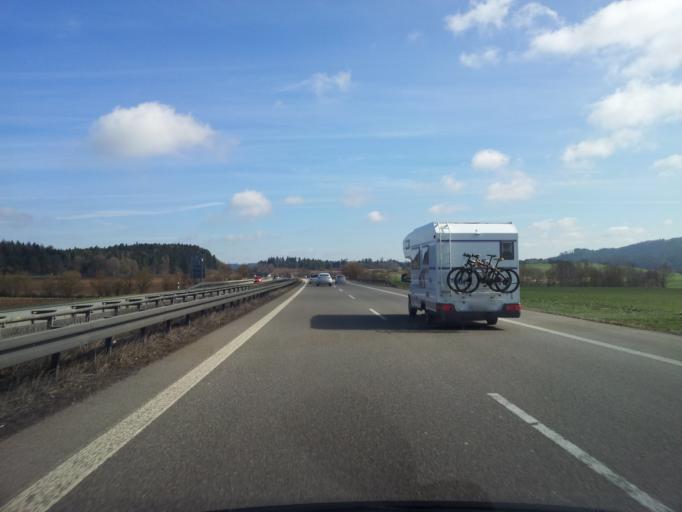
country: DE
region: Baden-Wuerttemberg
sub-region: Freiburg Region
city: Dietingen
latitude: 48.2104
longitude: 8.6332
